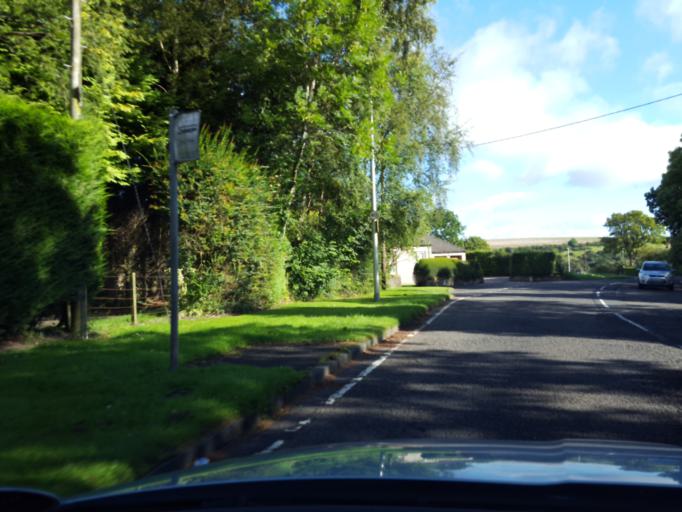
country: GB
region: Scotland
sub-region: West Lothian
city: Broxburn
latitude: 55.9422
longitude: -3.5086
